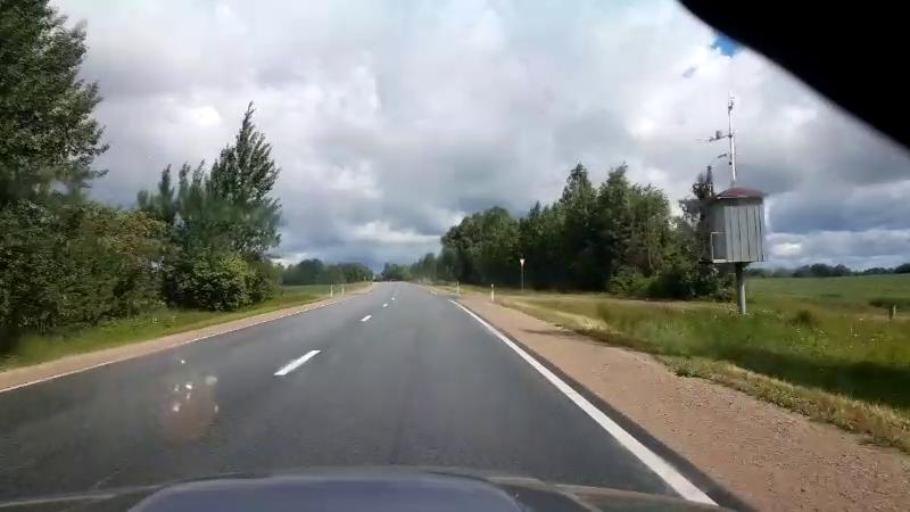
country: LV
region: Lecava
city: Iecava
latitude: 56.5233
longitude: 24.1722
